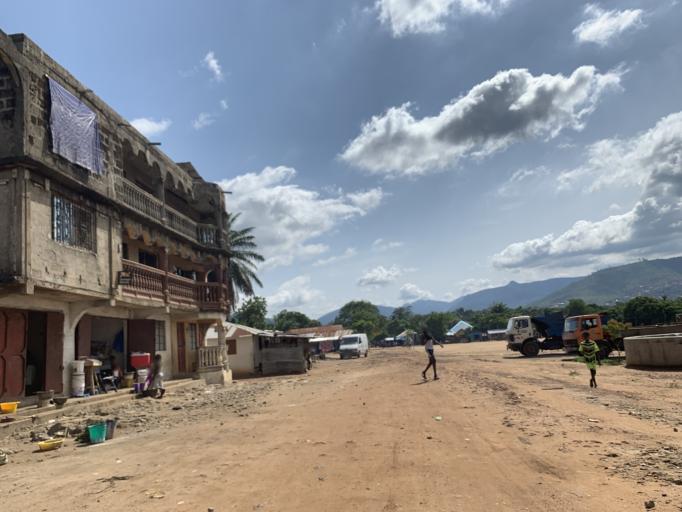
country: SL
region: Western Area
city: Waterloo
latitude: 8.3311
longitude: -13.0515
